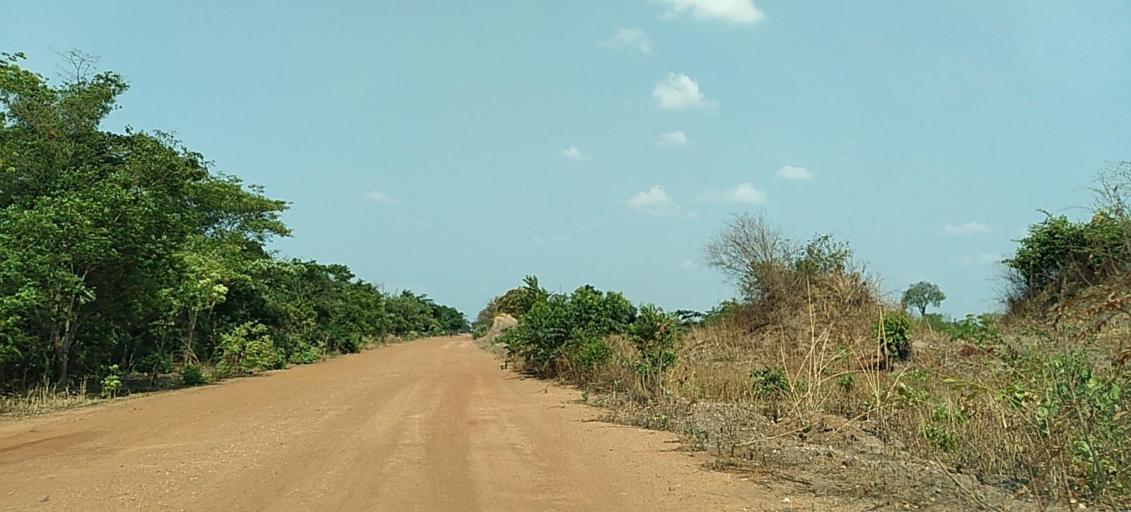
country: ZM
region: Copperbelt
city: Luanshya
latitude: -13.0911
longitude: 28.2882
